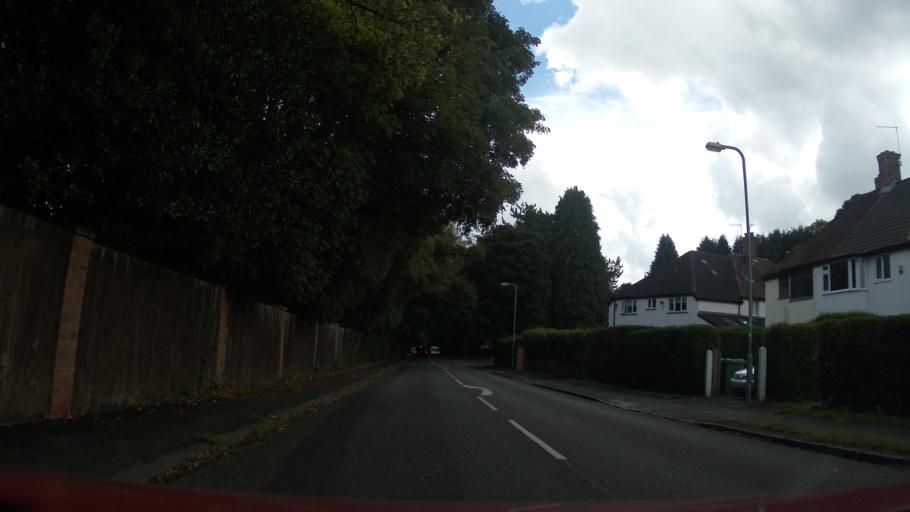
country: GB
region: England
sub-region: Stoke-on-Trent
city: Stoke-on-Trent
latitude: 52.9695
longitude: -2.2050
